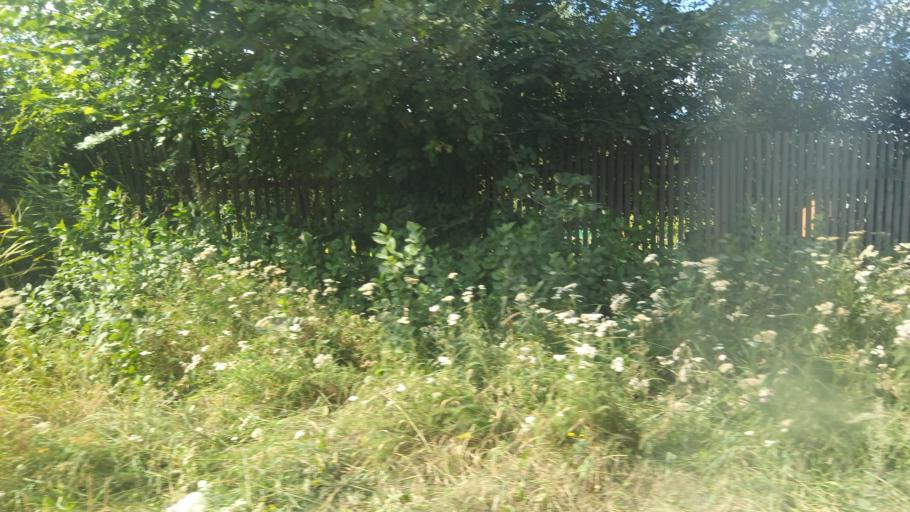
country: RU
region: Chelyabinsk
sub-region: Gorod Chelyabinsk
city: Chelyabinsk
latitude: 55.1250
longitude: 61.3916
